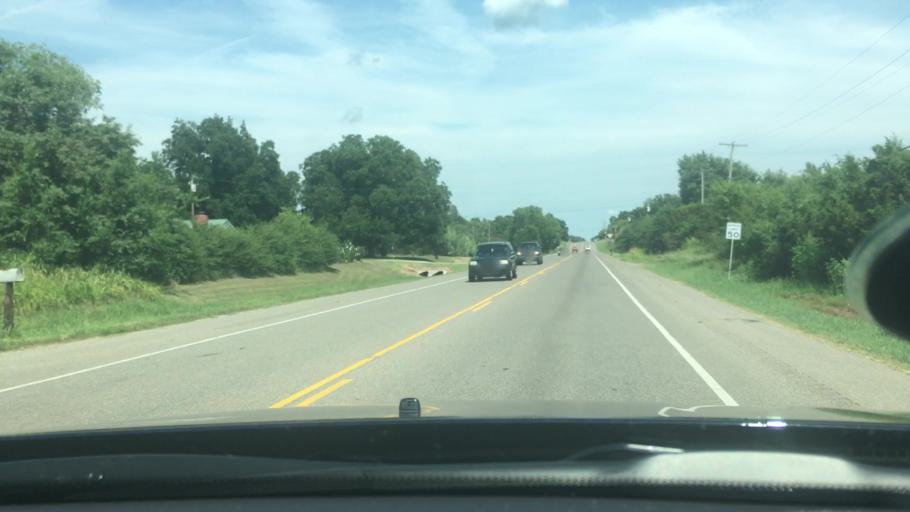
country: US
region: Oklahoma
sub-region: Pottawatomie County
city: Shawnee
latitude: 35.3331
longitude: -96.8569
